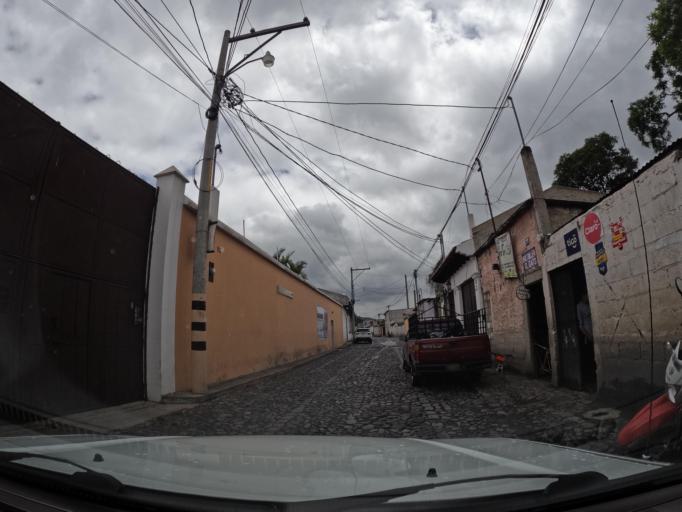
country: GT
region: Sacatepequez
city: Antigua Guatemala
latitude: 14.5672
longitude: -90.7411
